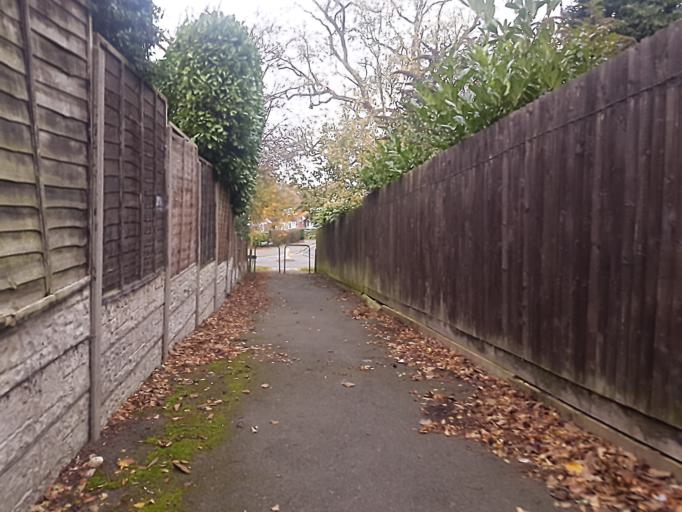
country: GB
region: England
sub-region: City and Borough of Birmingham
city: Acocks Green
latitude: 52.4356
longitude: -1.8004
